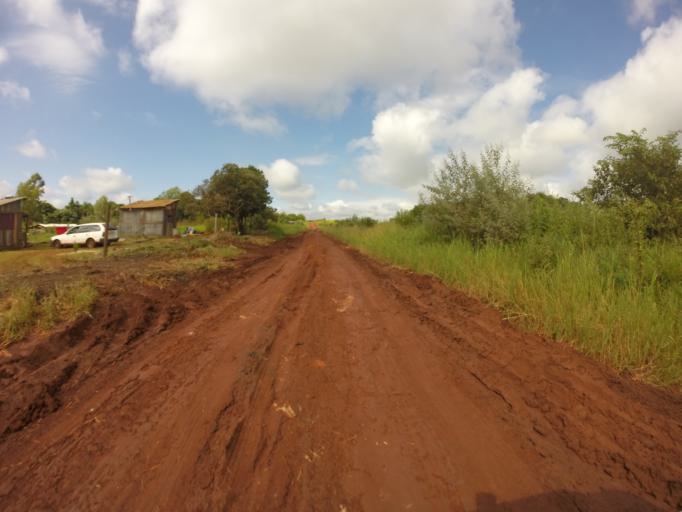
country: PY
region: Alto Parana
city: Ciudad del Este
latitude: -25.4036
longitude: -54.6583
